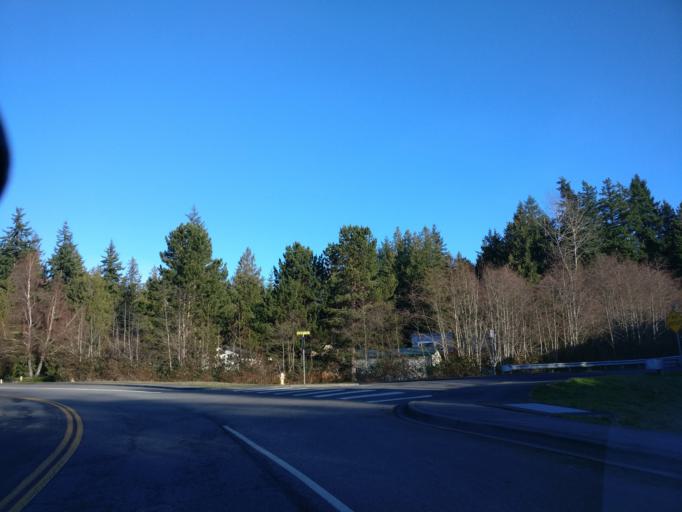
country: US
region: Washington
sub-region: Skagit County
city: Mount Vernon
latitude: 48.4137
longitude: -122.2977
